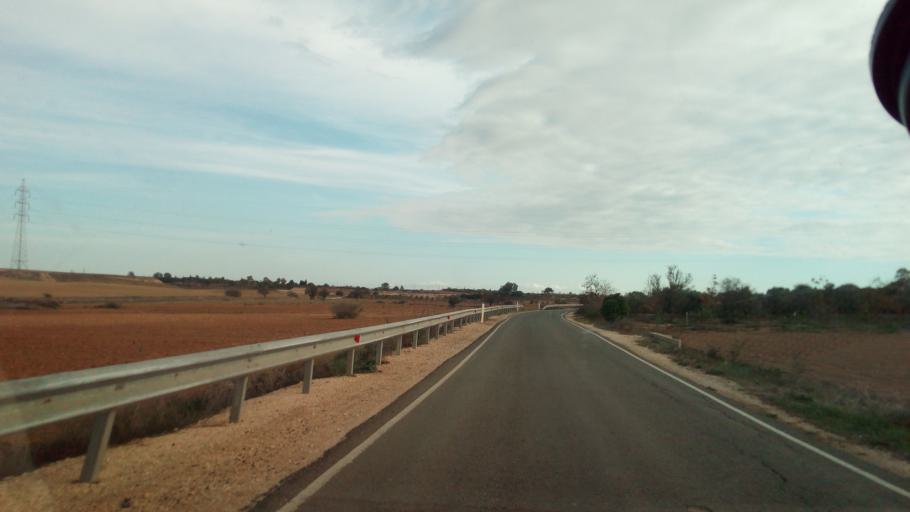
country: CY
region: Ammochostos
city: Frenaros
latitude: 35.0545
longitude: 33.8844
